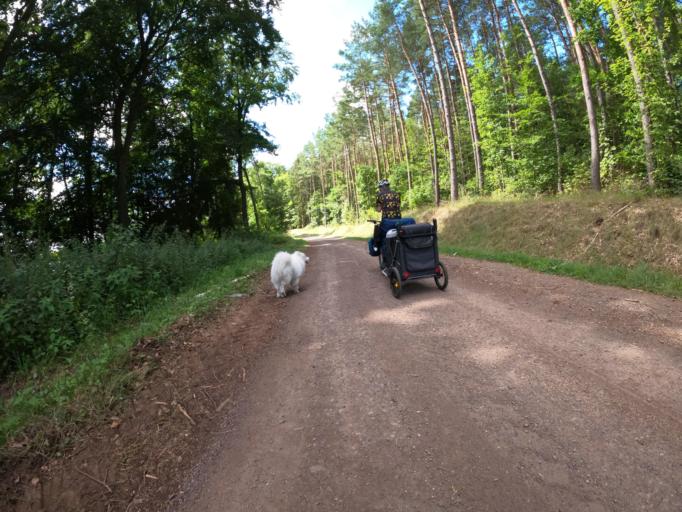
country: PL
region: West Pomeranian Voivodeship
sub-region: Powiat lobeski
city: Lobez
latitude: 53.6951
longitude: 15.5468
